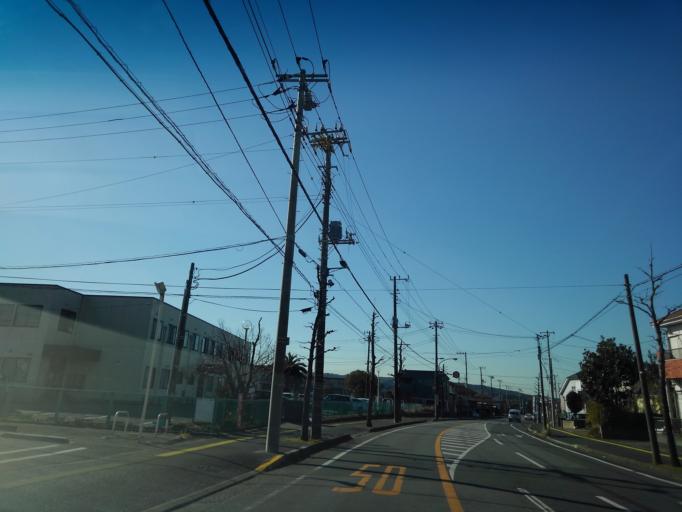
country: JP
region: Chiba
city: Kimitsu
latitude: 35.3258
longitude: 139.9123
